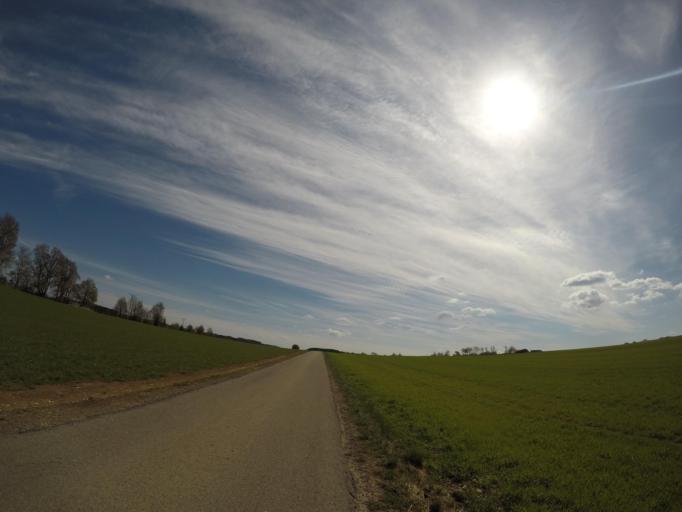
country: DE
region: Baden-Wuerttemberg
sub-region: Tuebingen Region
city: Mehrstetten
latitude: 48.3454
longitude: 9.5623
